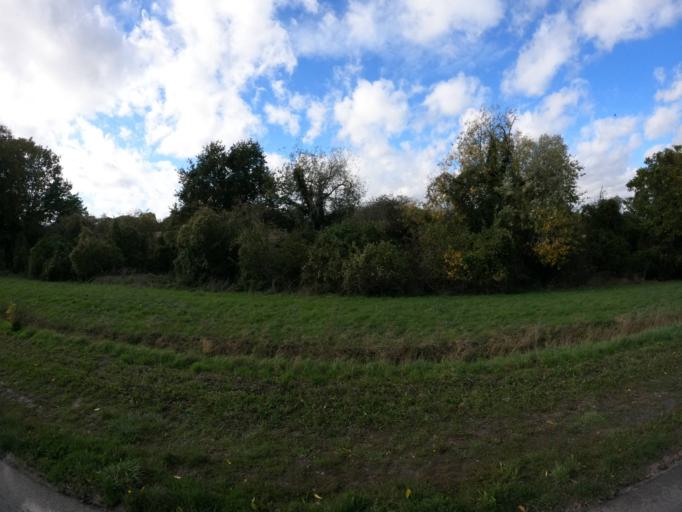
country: FR
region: Ile-de-France
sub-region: Departement de Seine-et-Marne
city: Coupvray
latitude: 48.8916
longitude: 2.8081
